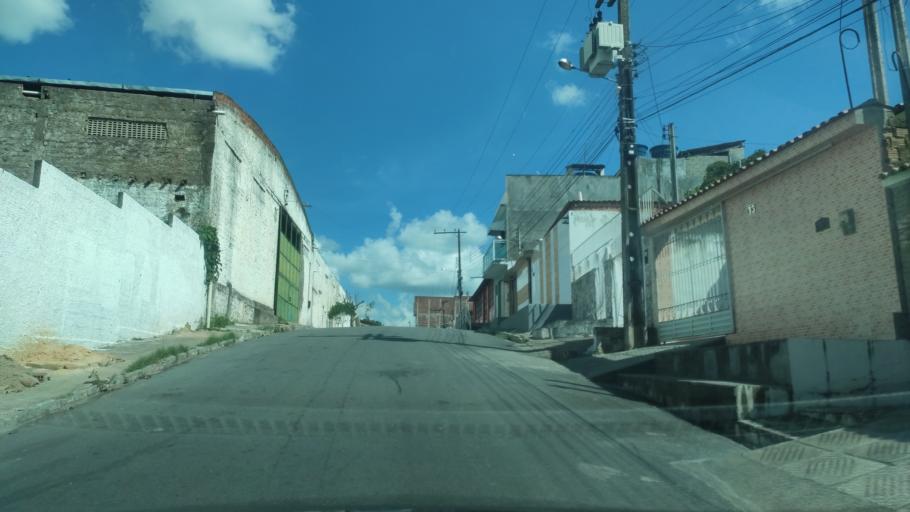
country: BR
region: Alagoas
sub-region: Uniao Dos Palmares
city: Uniao dos Palmares
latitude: -9.1600
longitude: -36.0352
